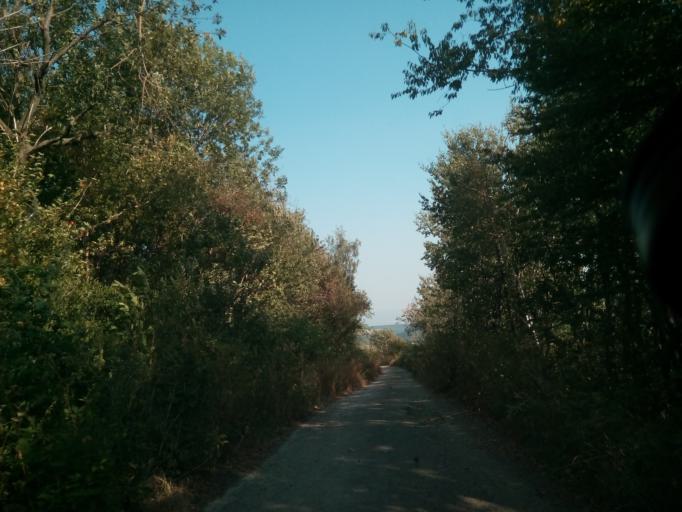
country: SK
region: Kosicky
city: Moldava nad Bodvou
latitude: 48.7341
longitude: 21.0961
